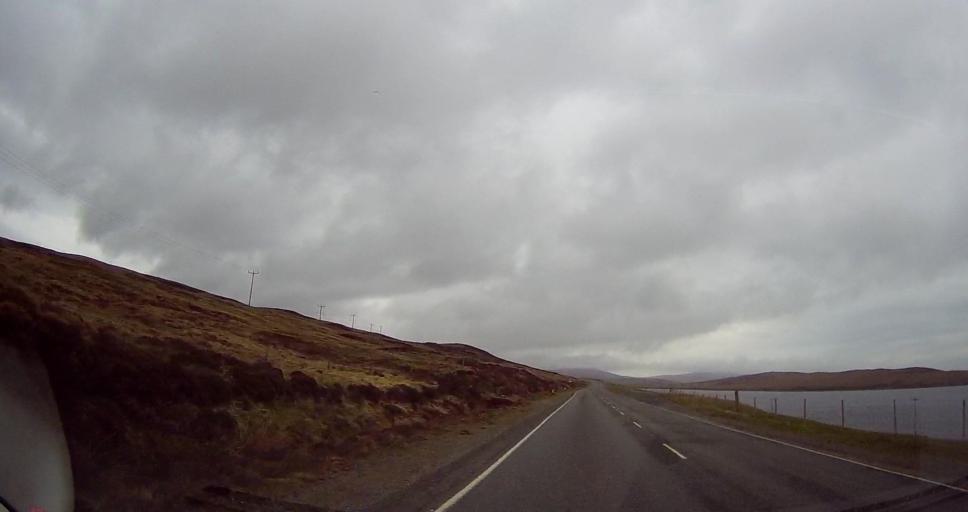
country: GB
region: Scotland
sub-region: Shetland Islands
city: Lerwick
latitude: 60.2463
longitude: -1.2282
